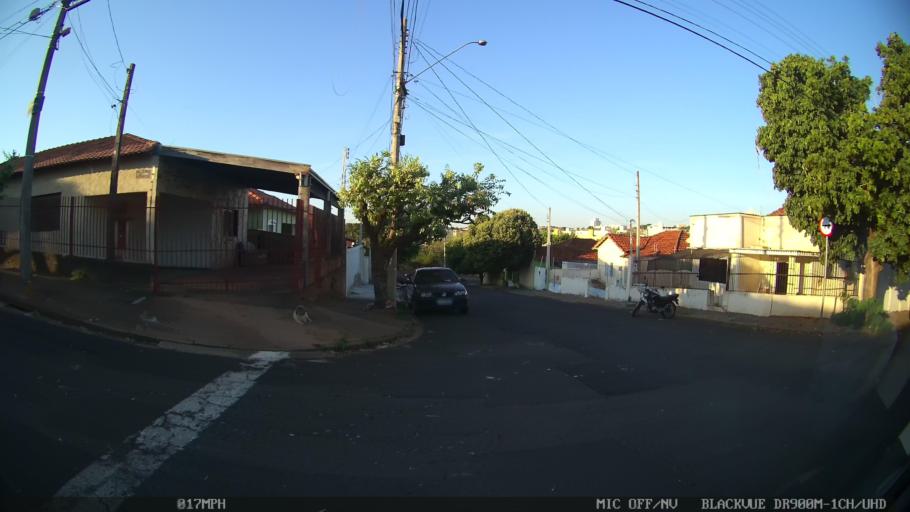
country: BR
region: Sao Paulo
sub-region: Sao Jose Do Rio Preto
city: Sao Jose do Rio Preto
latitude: -20.8018
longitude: -49.3798
